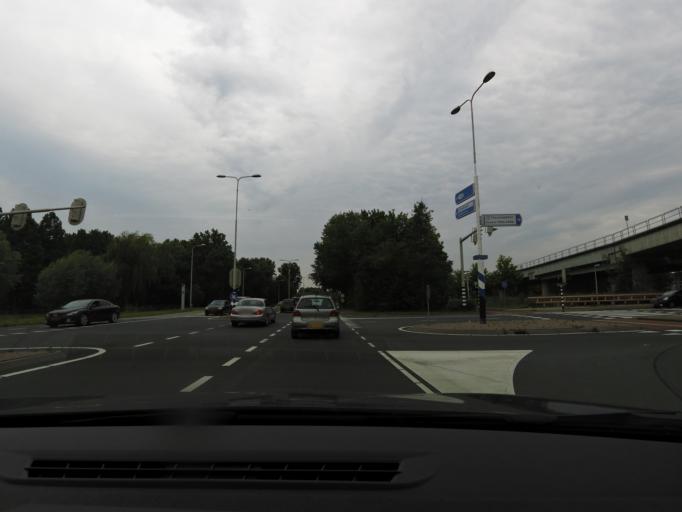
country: NL
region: South Holland
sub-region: Gemeente Albrandswaard
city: Rhoon
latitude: 51.8625
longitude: 4.3755
